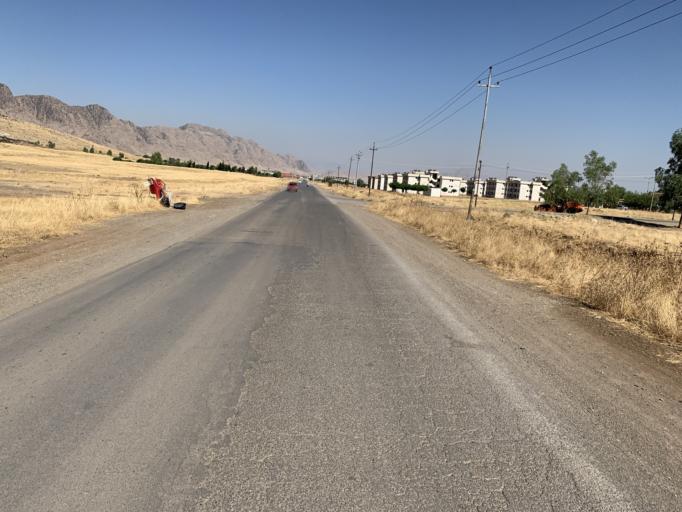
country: IQ
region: As Sulaymaniyah
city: Raniye
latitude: 36.2656
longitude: 44.8416
